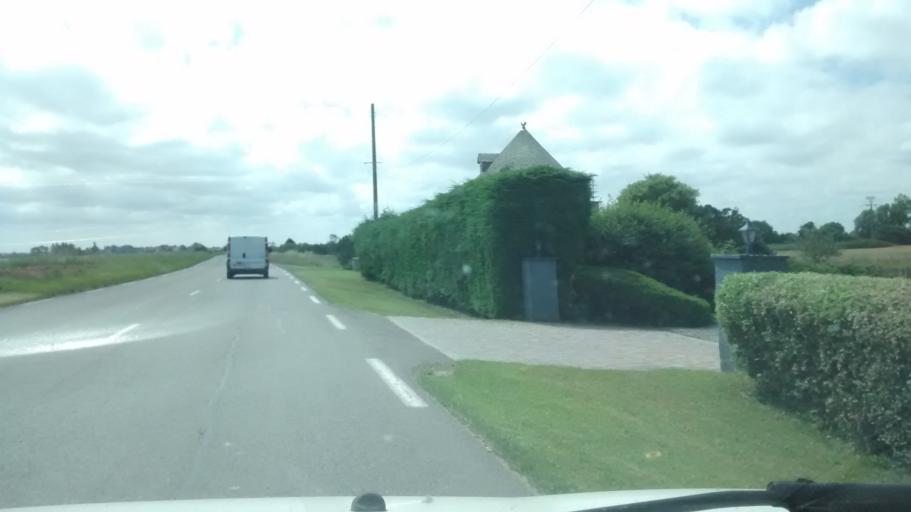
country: FR
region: Brittany
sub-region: Departement d'Ille-et-Vilaine
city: La Gouesniere
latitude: 48.6310
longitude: -1.8637
